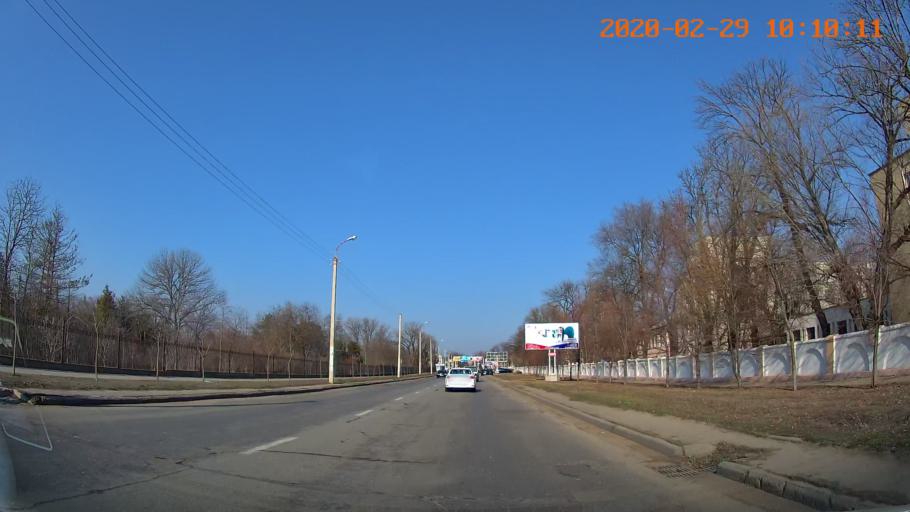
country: MD
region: Telenesti
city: Tiraspolul Nou
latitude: 46.8318
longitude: 29.6462
